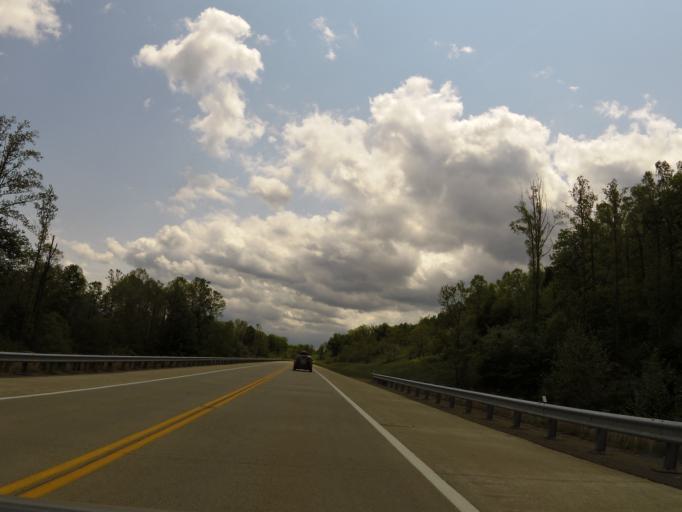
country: US
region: Ohio
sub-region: Athens County
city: Athens
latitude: 39.2131
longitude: -82.0627
